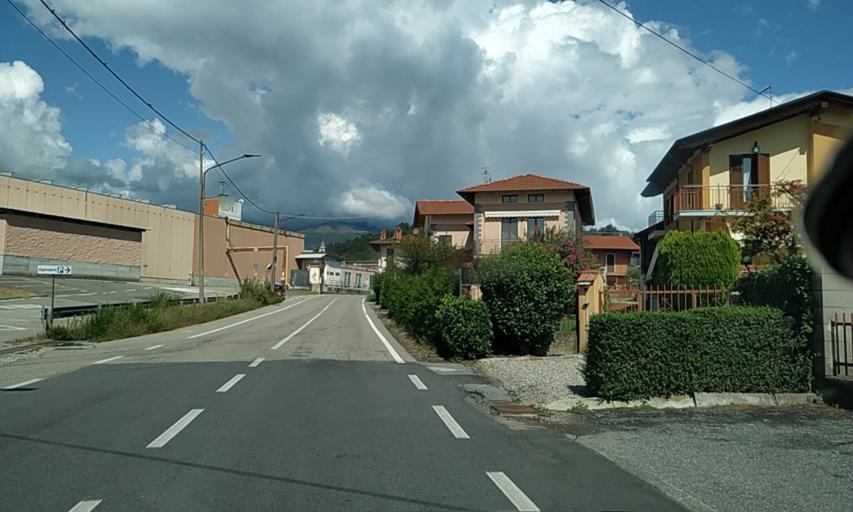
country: IT
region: Piedmont
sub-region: Provincia di Biella
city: Ceresane-Curanuova
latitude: 45.5247
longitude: 8.0052
